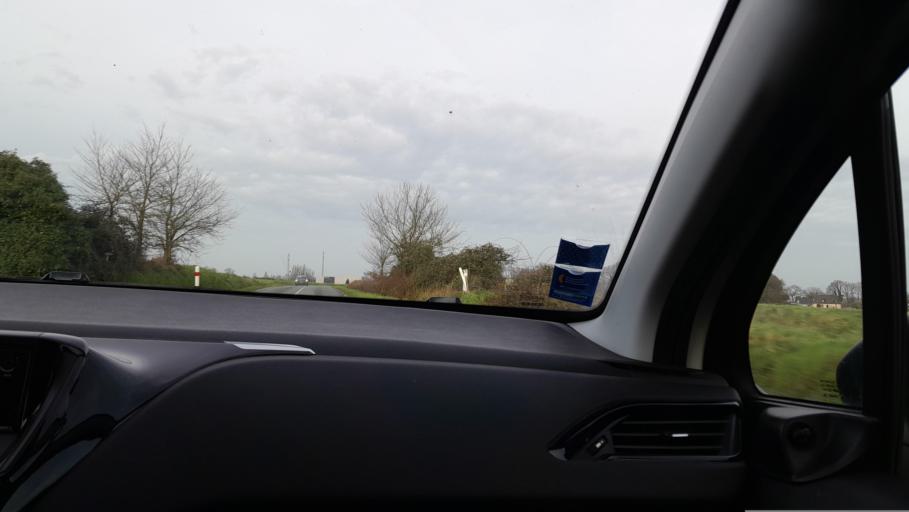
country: FR
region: Brittany
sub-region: Departement d'Ille-et-Vilaine
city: La Guerche-de-Bretagne
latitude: 47.9294
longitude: -1.2183
